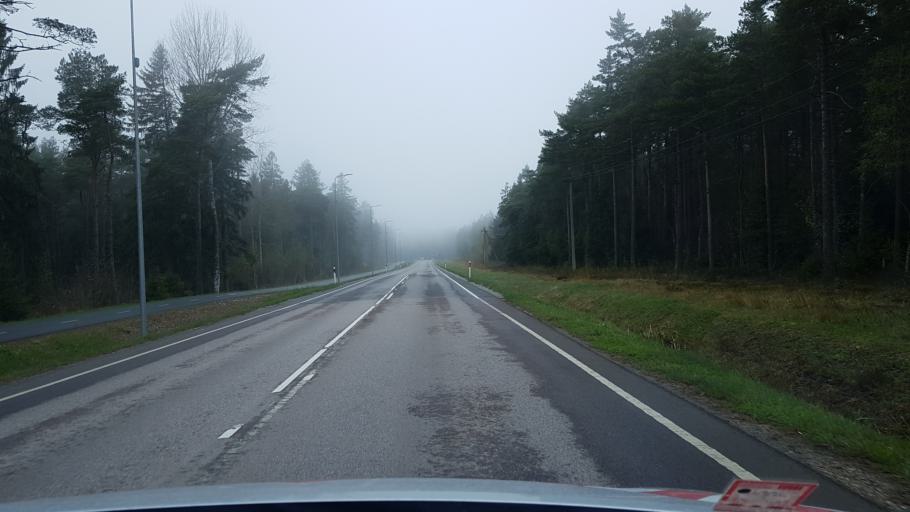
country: EE
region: Harju
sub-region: Viimsi vald
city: Viimsi
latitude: 59.5181
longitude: 24.8990
